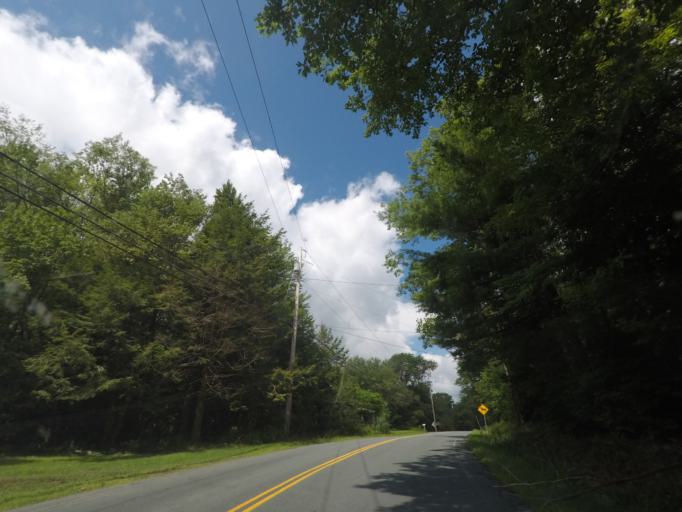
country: US
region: New York
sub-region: Rensselaer County
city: Averill Park
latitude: 42.6459
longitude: -73.4933
